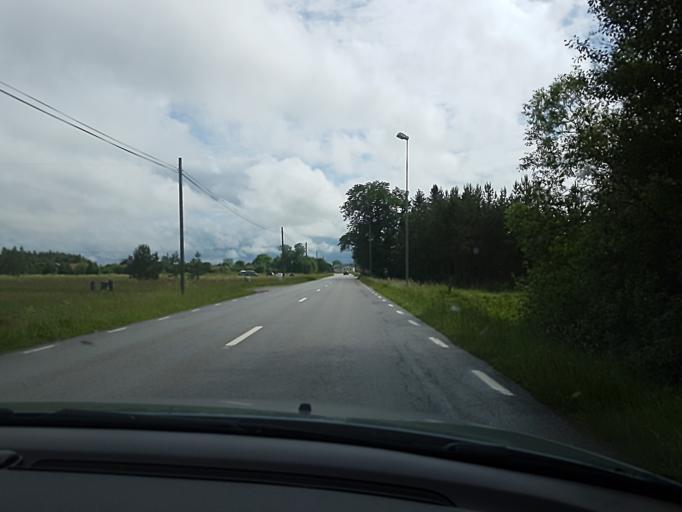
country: SE
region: Uppsala
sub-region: Osthammars Kommun
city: OEsthammar
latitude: 60.2923
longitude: 18.2847
